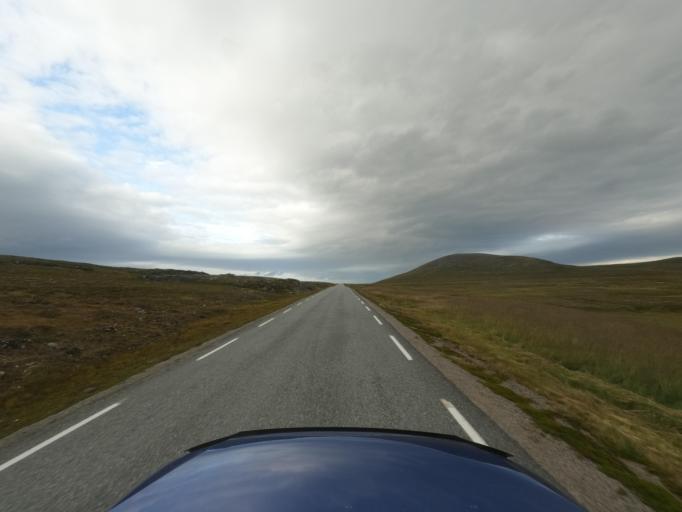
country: NO
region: Finnmark Fylke
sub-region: Nordkapp
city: Honningsvag
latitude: 70.8445
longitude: 25.7916
